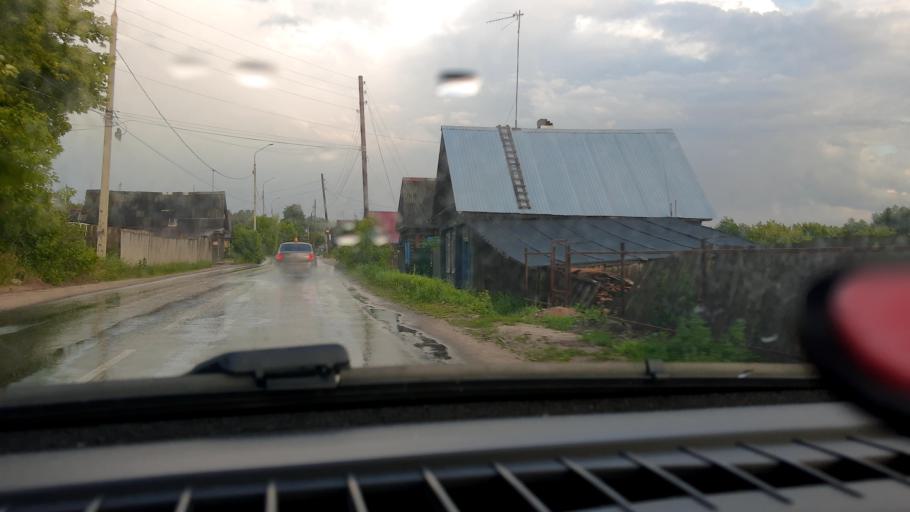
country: RU
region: Nizjnij Novgorod
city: Gorodets
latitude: 56.6609
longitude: 43.4610
